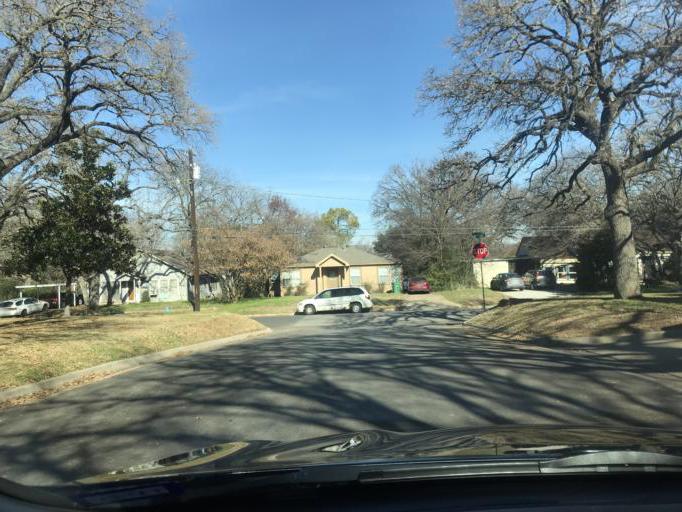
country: US
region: Texas
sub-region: Denton County
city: Denton
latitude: 33.2202
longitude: -97.1488
